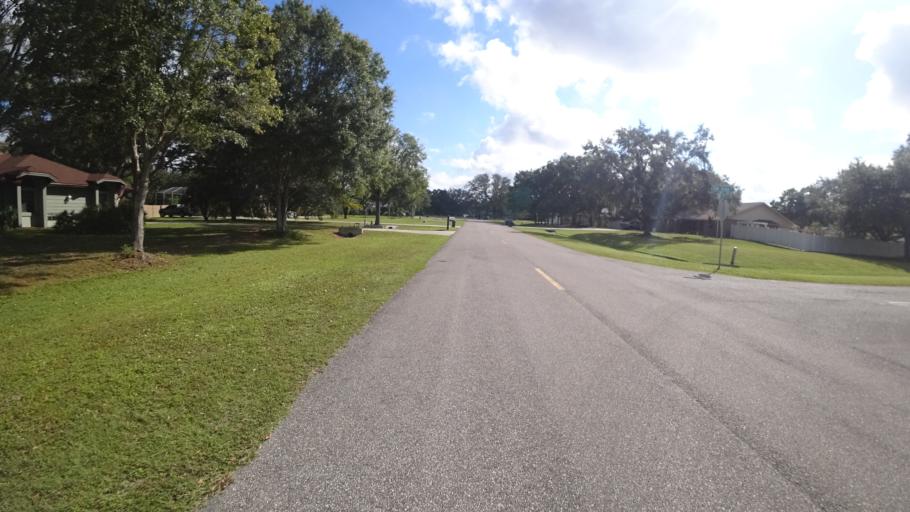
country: US
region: Florida
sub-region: Sarasota County
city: North Sarasota
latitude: 27.3985
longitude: -82.5206
